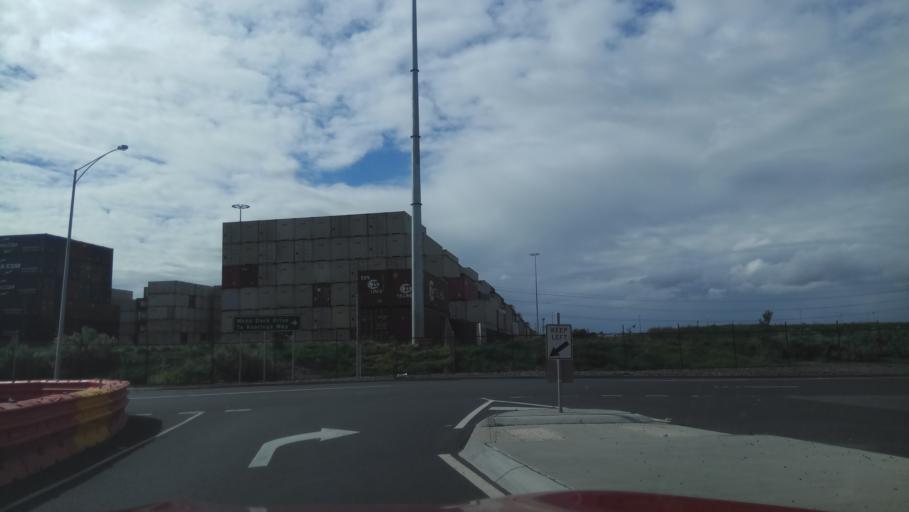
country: AU
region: Victoria
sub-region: Hobsons Bay
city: Williamstown
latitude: -37.8377
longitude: 144.9120
